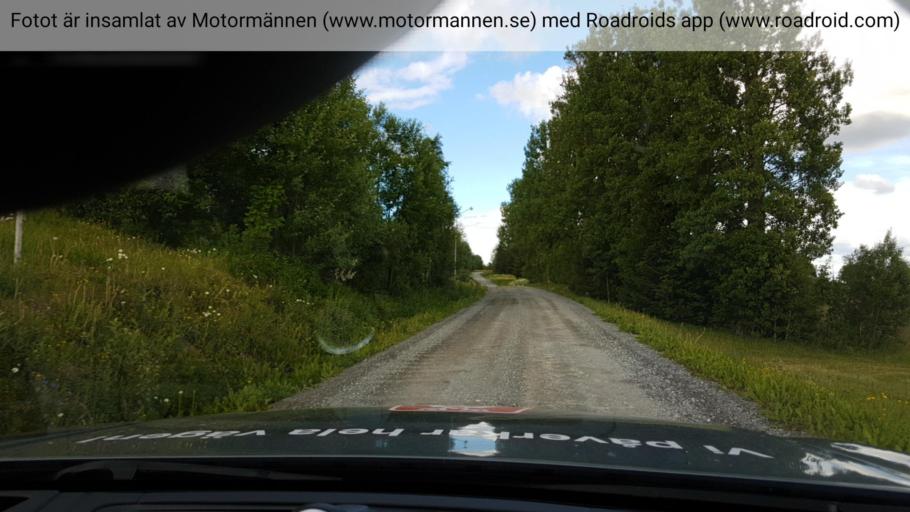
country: SE
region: Jaemtland
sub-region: Bergs Kommun
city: Hoverberg
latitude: 62.9603
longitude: 14.2657
